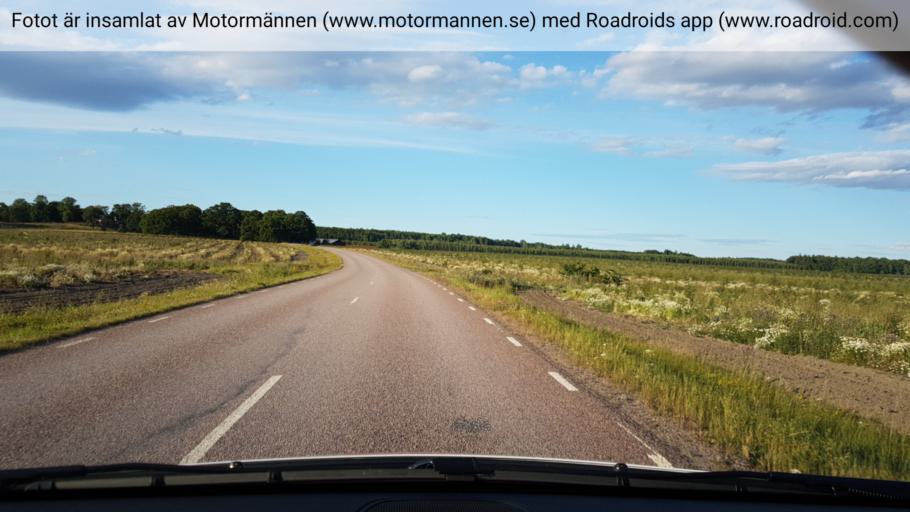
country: SE
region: Vaestmanland
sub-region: Vasteras
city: Tillberga
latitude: 59.7054
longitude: 16.6556
